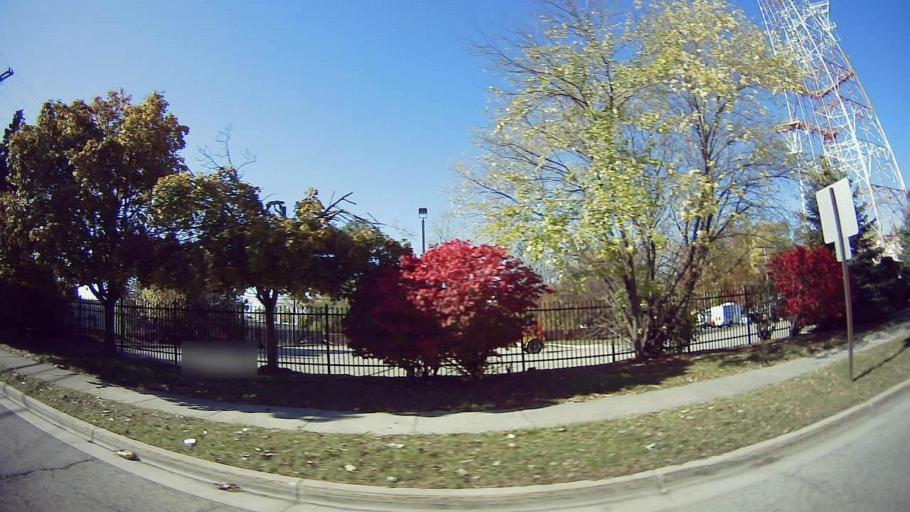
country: US
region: Michigan
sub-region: Oakland County
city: Southfield
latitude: 42.4733
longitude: -83.2609
